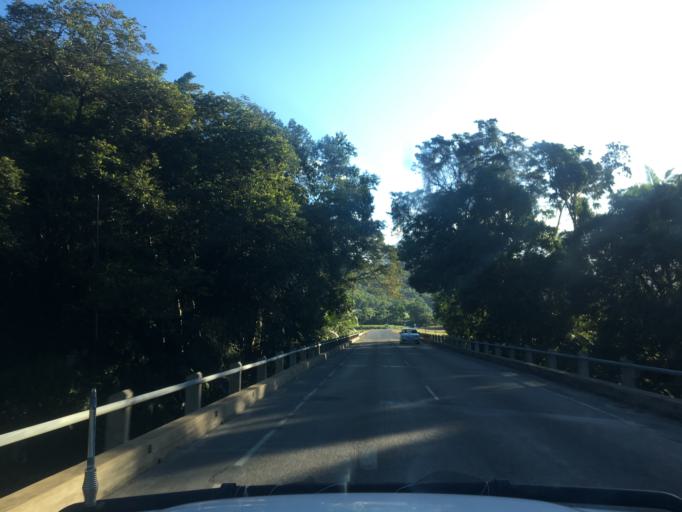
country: AU
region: Queensland
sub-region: Cairns
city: Port Douglas
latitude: -16.4843
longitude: 145.3843
